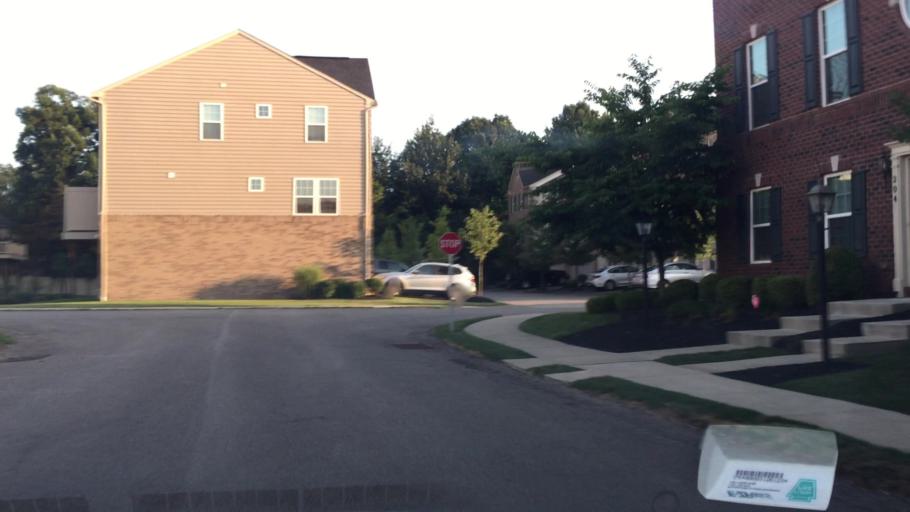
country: US
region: Pennsylvania
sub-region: Butler County
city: Seven Fields
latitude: 40.6810
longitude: -80.0403
